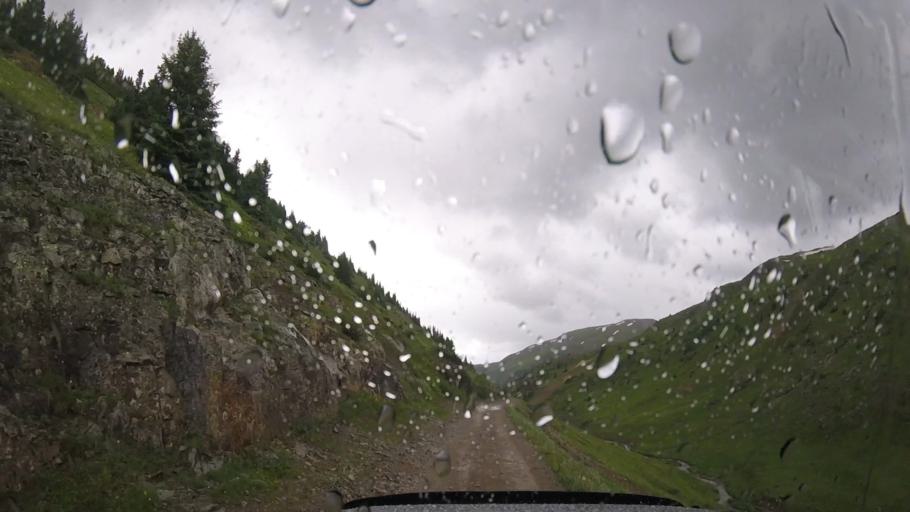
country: US
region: Colorado
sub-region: Ouray County
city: Ouray
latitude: 37.9448
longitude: -107.5740
